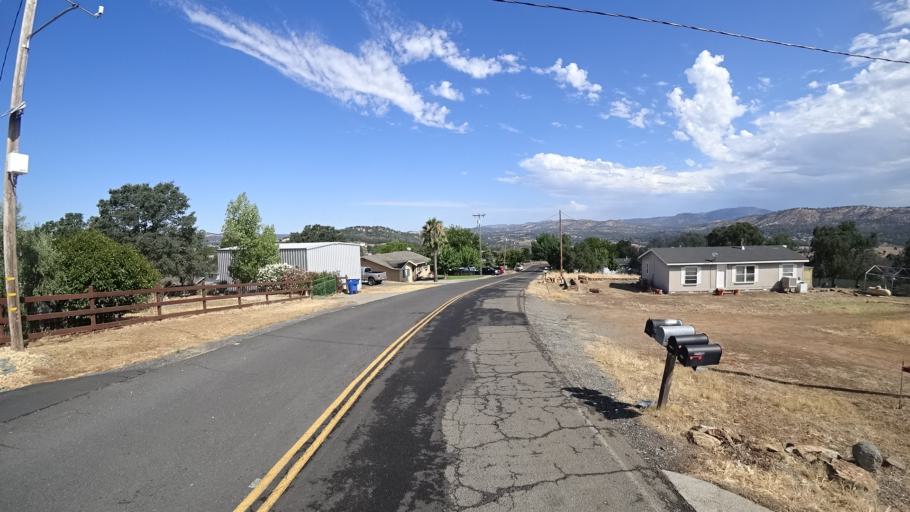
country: US
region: California
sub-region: Calaveras County
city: Copperopolis
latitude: 37.9135
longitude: -120.6141
